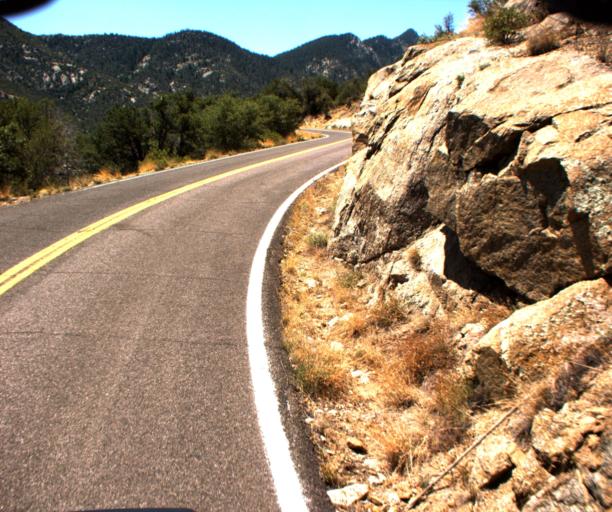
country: US
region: Arizona
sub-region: Graham County
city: Swift Trail Junction
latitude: 32.6620
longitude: -109.8010
